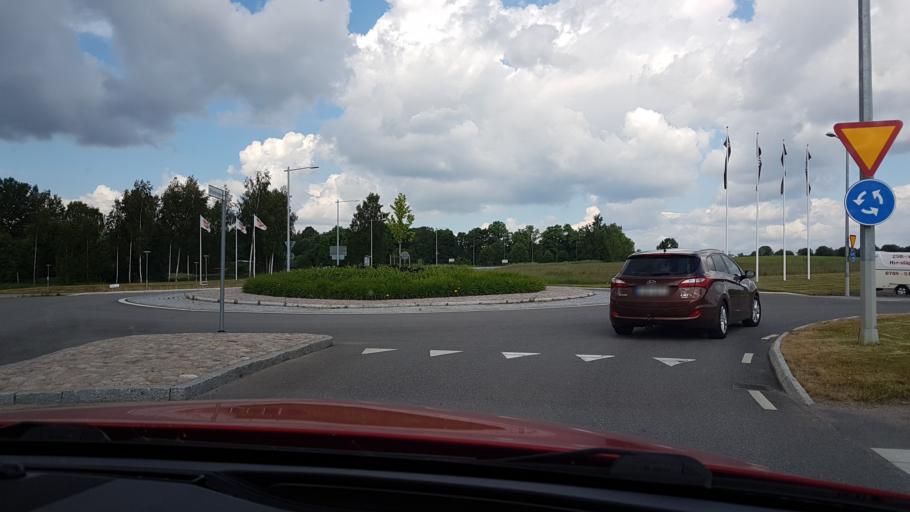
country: SE
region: Vaestra Goetaland
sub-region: Hjo Kommun
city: Hjo
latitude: 58.3135
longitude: 14.2767
